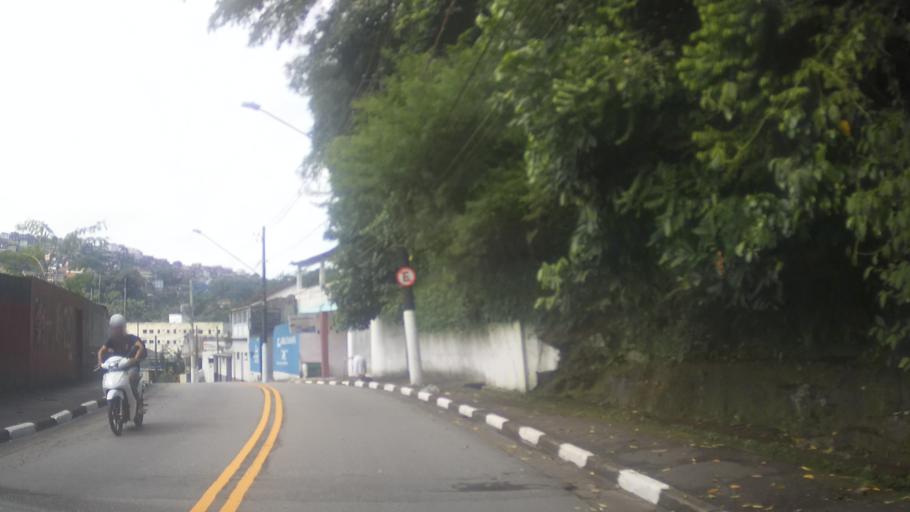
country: BR
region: Sao Paulo
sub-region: Santos
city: Santos
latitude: -23.9465
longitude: -46.3528
